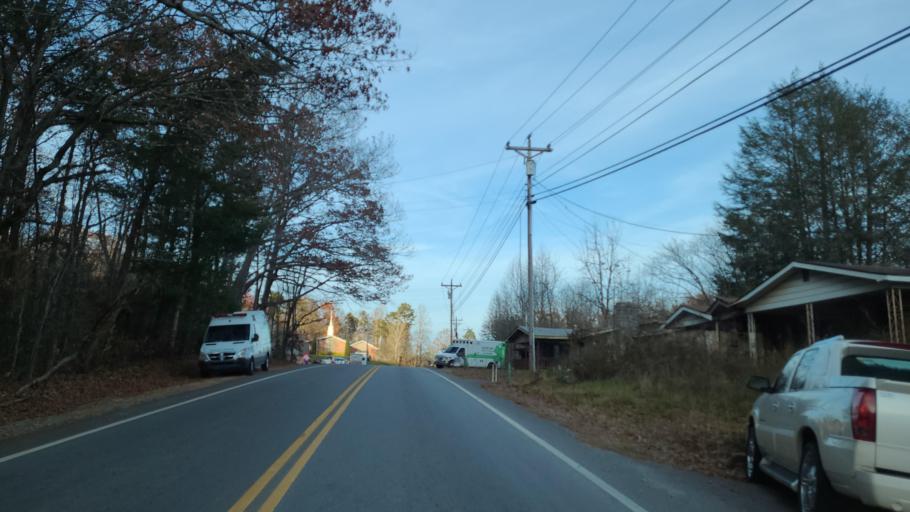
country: US
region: Georgia
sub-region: Union County
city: Blairsville
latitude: 34.8700
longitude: -83.9499
